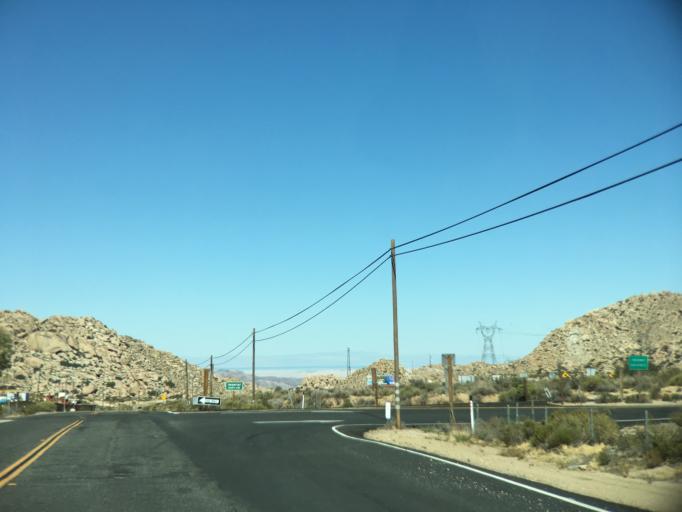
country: MX
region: Baja California
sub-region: Tecate
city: Cereso del Hongo
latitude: 32.6460
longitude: -116.1063
